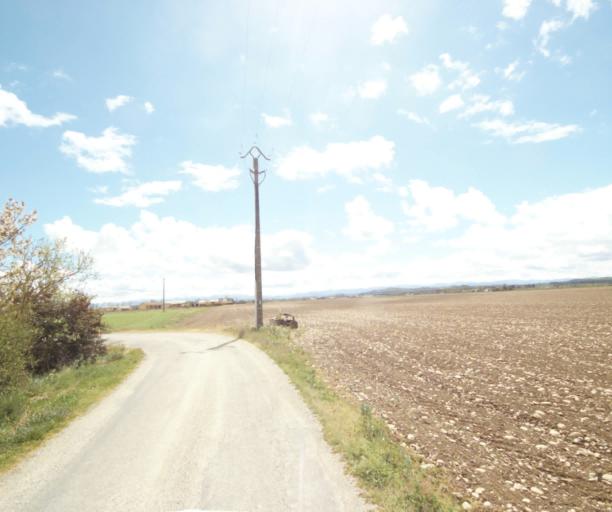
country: FR
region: Midi-Pyrenees
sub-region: Departement de l'Ariege
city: Saverdun
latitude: 43.2432
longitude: 1.6098
